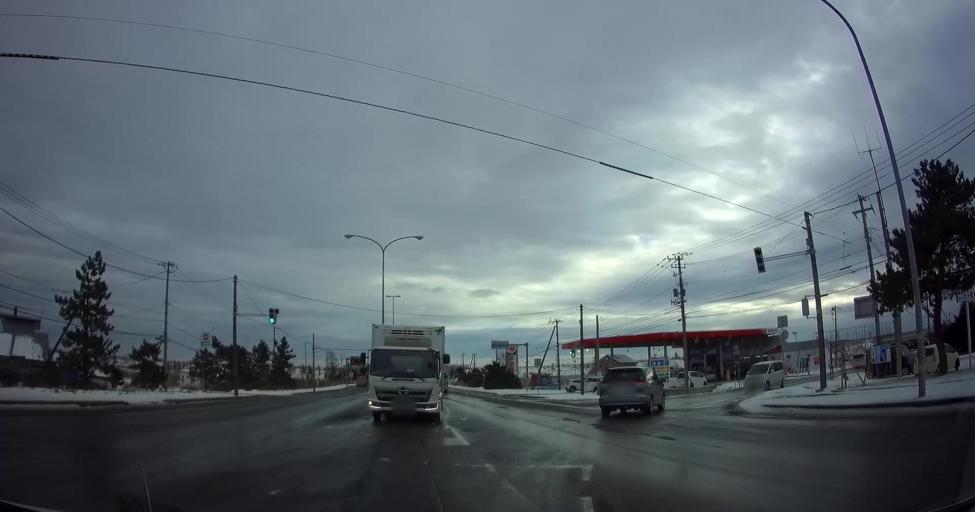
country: JP
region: Hokkaido
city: Nanae
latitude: 41.8371
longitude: 140.6918
